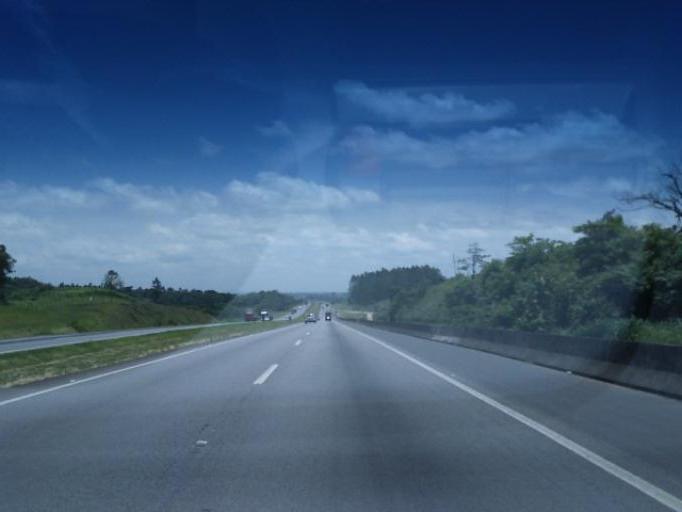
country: BR
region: Sao Paulo
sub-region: Registro
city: Registro
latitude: -24.4672
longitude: -47.8213
